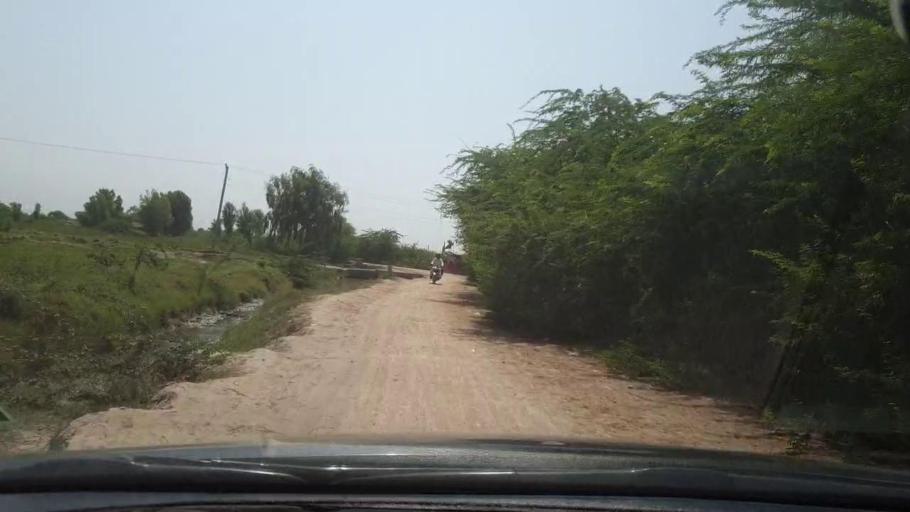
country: PK
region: Sindh
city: Tando Bago
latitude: 24.7776
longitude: 69.1832
